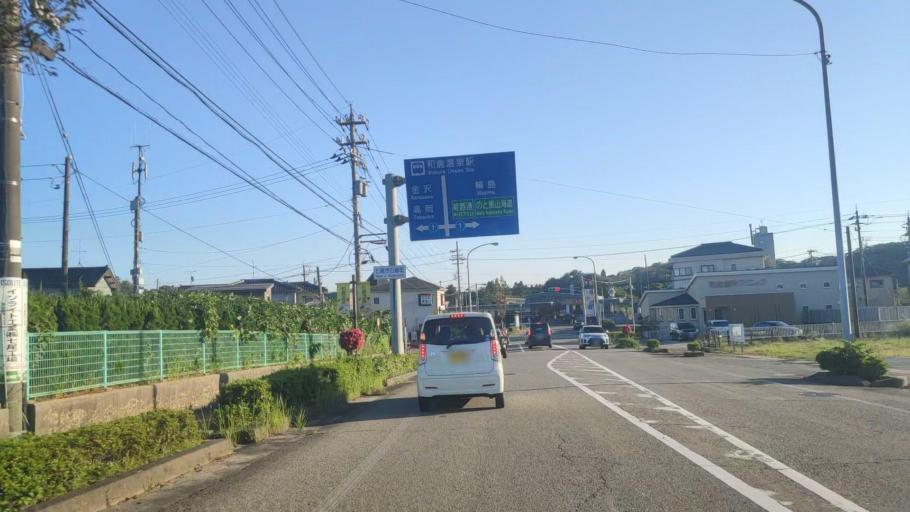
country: JP
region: Ishikawa
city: Nanao
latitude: 37.0764
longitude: 136.9258
